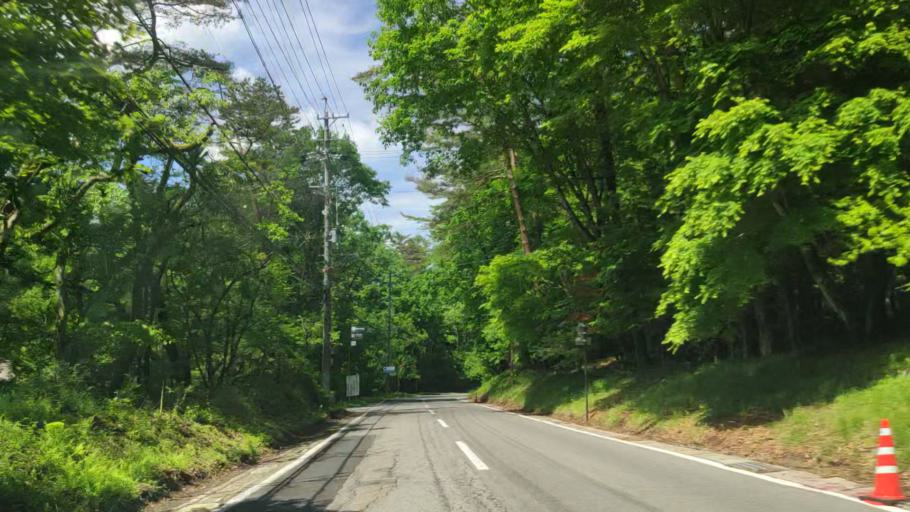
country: JP
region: Nagano
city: Chino
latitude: 36.0596
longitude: 138.2733
